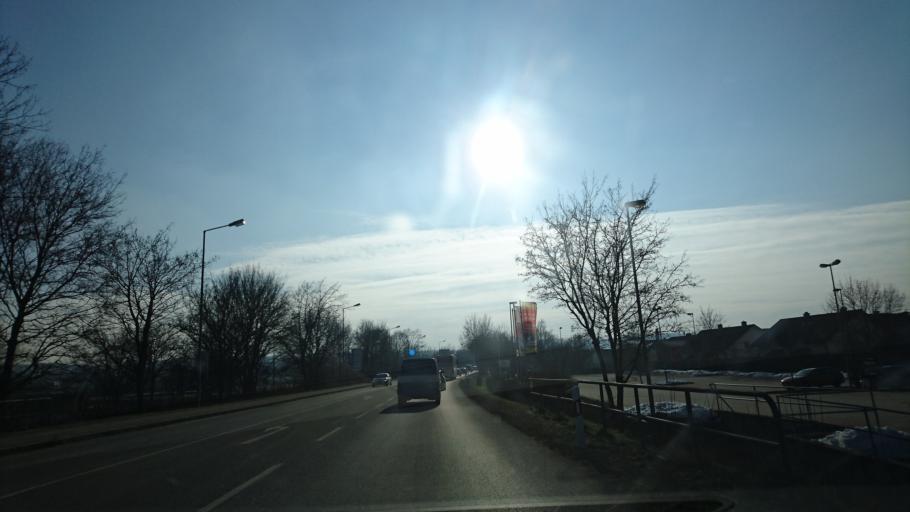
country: DE
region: Bavaria
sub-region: Lower Bavaria
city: Pfarrkirchen
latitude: 48.4279
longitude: 12.9431
